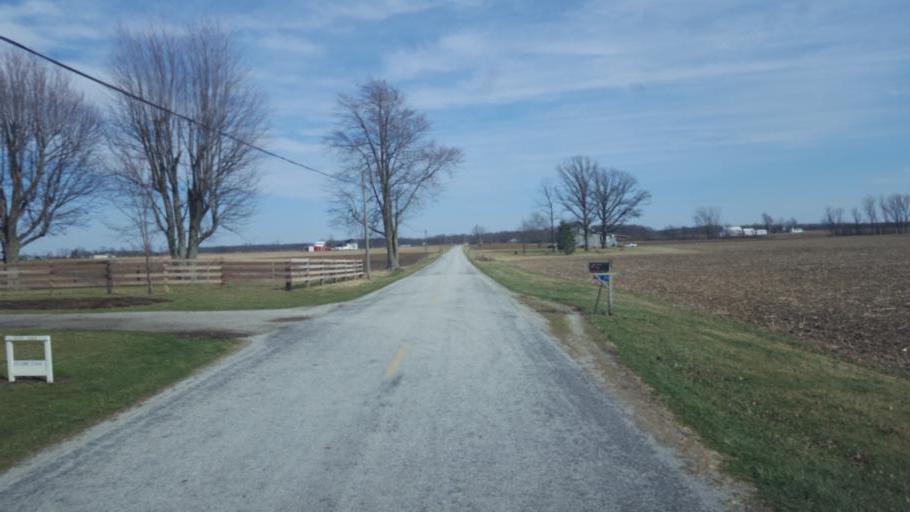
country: US
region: Ohio
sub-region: Hardin County
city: Kenton
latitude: 40.6578
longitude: -83.4667
